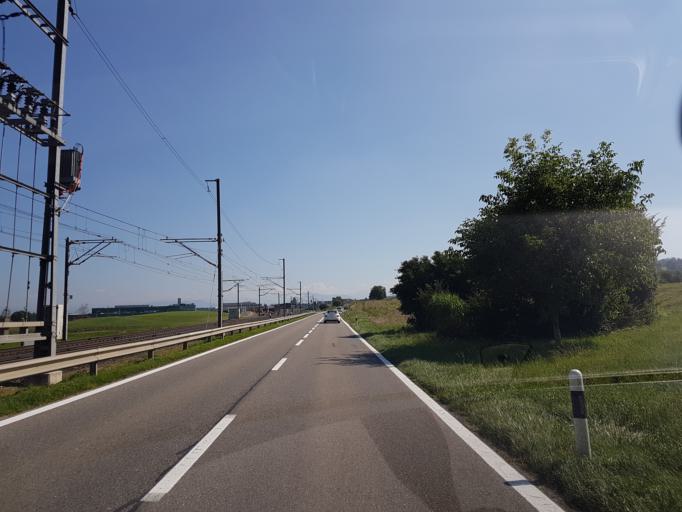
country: CH
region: Aargau
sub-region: Bezirk Muri
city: Waltenschwil
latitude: 47.3137
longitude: 8.3068
